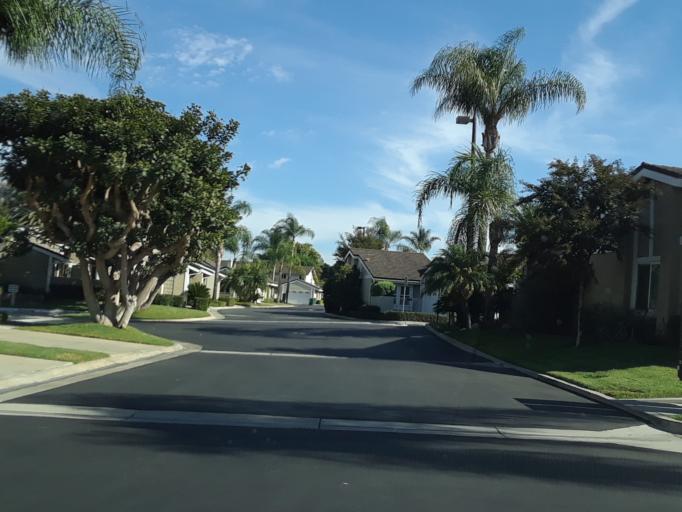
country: US
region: California
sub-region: Orange County
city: Irvine
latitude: 33.6766
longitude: -117.7891
